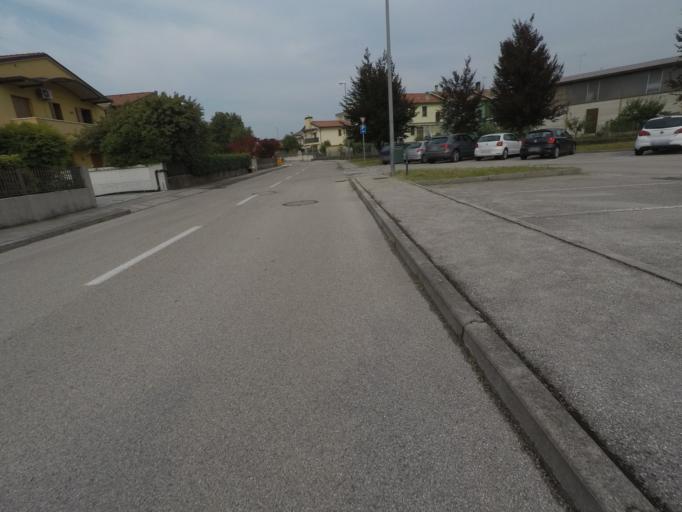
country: IT
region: Veneto
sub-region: Provincia di Treviso
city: Sarmede
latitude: 45.9751
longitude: 12.3811
